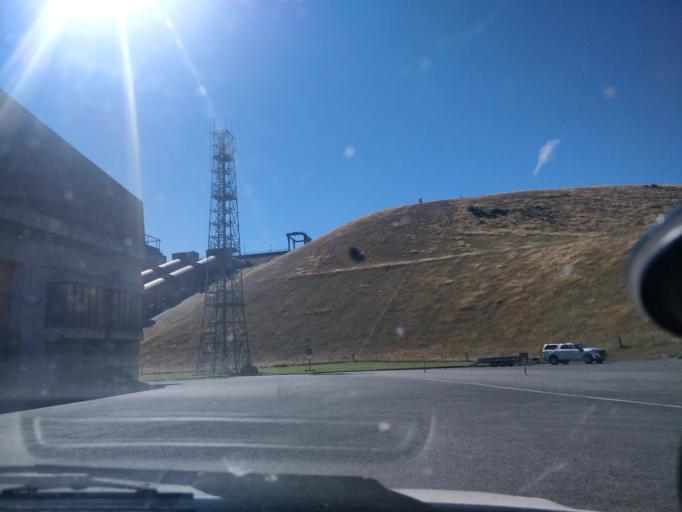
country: NZ
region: Otago
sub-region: Queenstown-Lakes District
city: Wanaka
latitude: -44.2651
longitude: 170.0330
